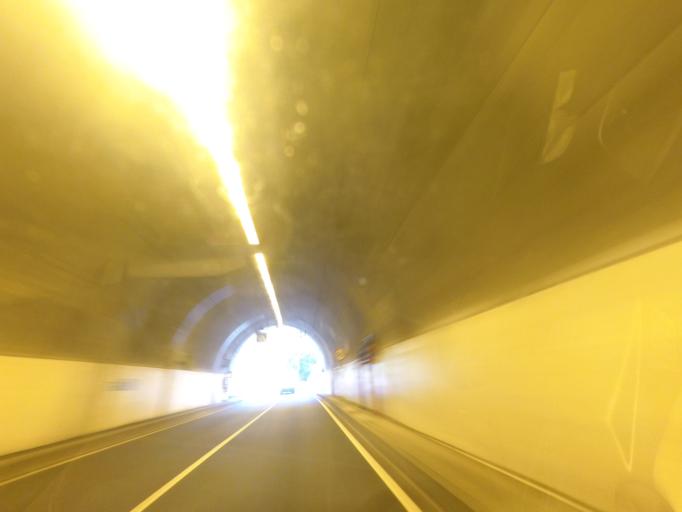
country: PT
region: Madeira
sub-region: Calheta
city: Estreito da Calheta
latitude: 32.7312
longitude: -17.1790
